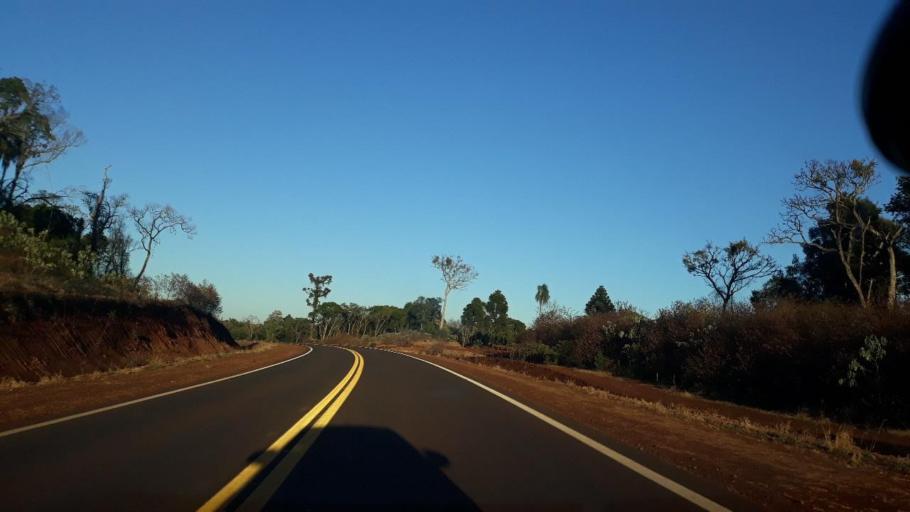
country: AR
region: Misiones
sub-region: Departamento de San Pedro
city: San Pedro
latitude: -26.5366
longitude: -53.9558
